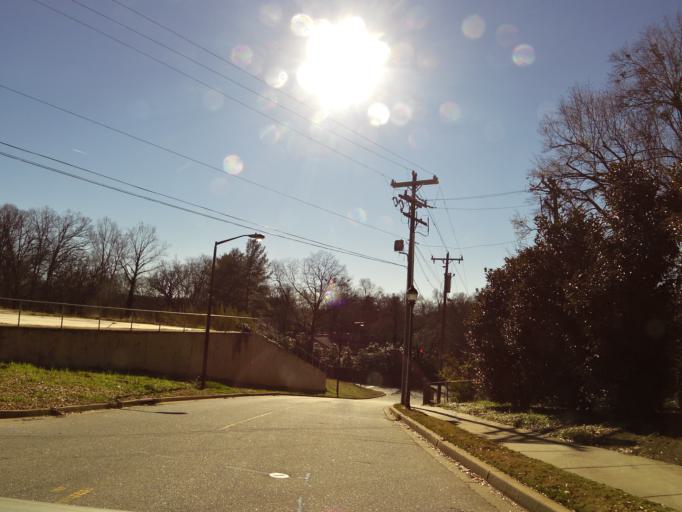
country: US
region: South Carolina
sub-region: Greenville County
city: Greenville
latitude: 34.8463
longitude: -82.3934
